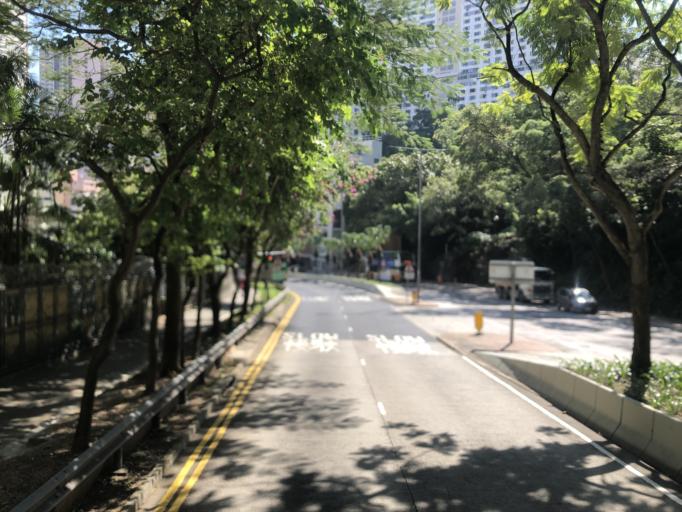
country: HK
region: Wanchai
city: Wan Chai
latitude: 22.2660
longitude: 114.2338
